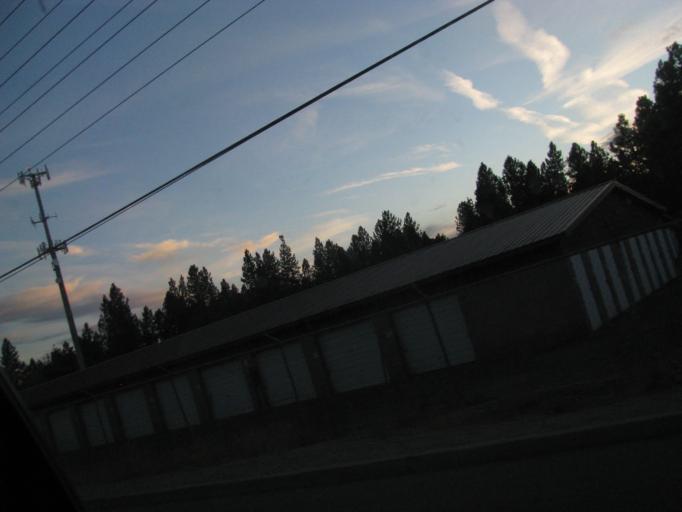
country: US
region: Washington
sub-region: Spokane County
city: Mead
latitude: 47.7994
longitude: -117.3497
